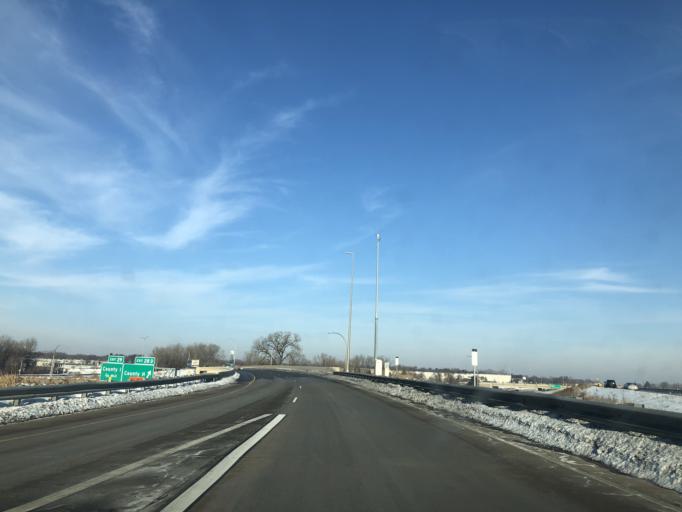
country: US
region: Minnesota
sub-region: Ramsey County
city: Mounds View
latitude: 45.0910
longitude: -93.1873
